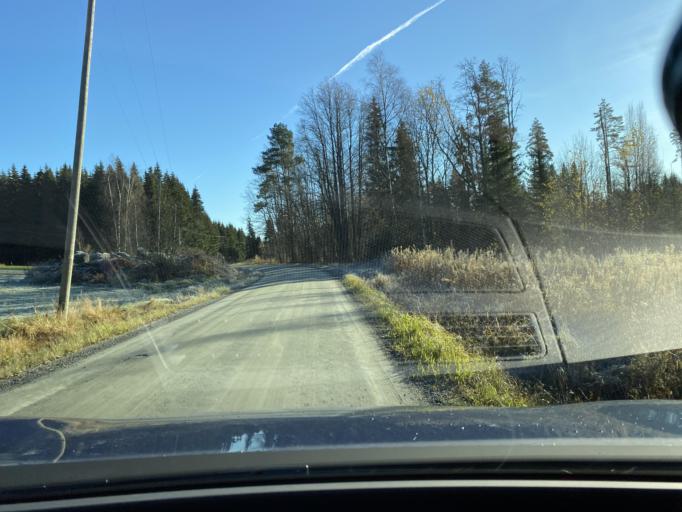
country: FI
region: Pirkanmaa
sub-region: Etelae-Pirkanmaa
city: Toijala
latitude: 61.0255
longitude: 23.8271
